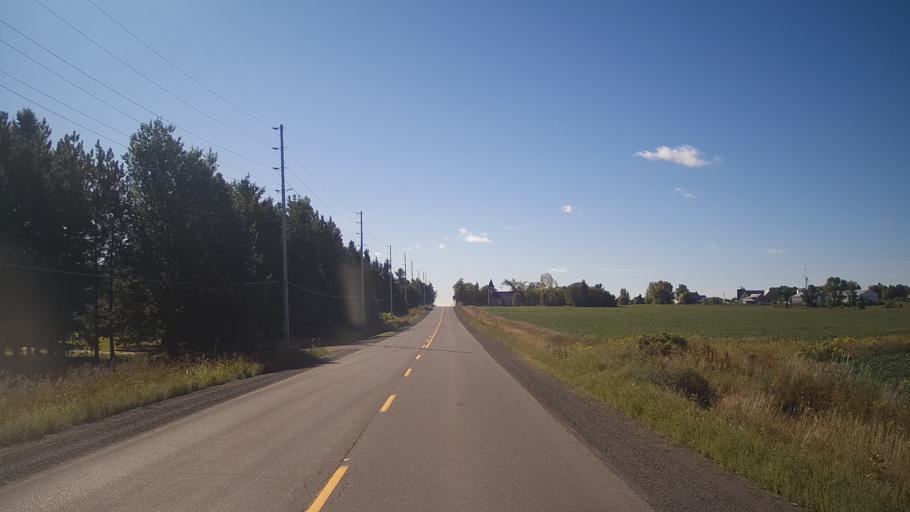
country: CA
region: Ontario
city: Prescott
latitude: 44.9735
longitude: -75.5350
